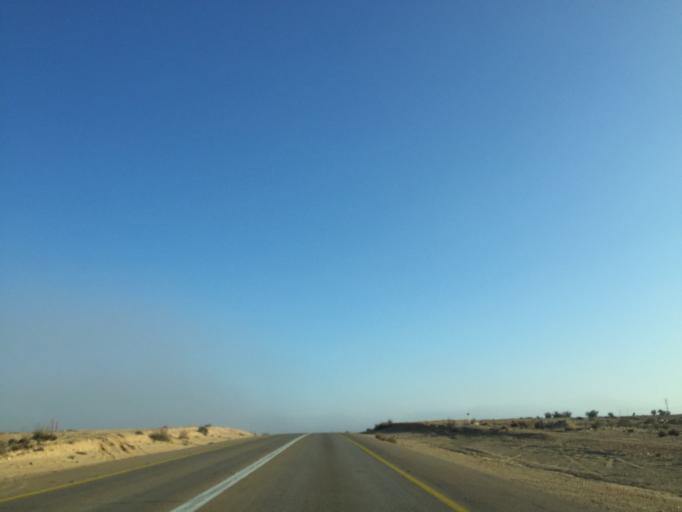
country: IL
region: Southern District
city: Yeroham
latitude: 31.0036
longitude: 34.9478
